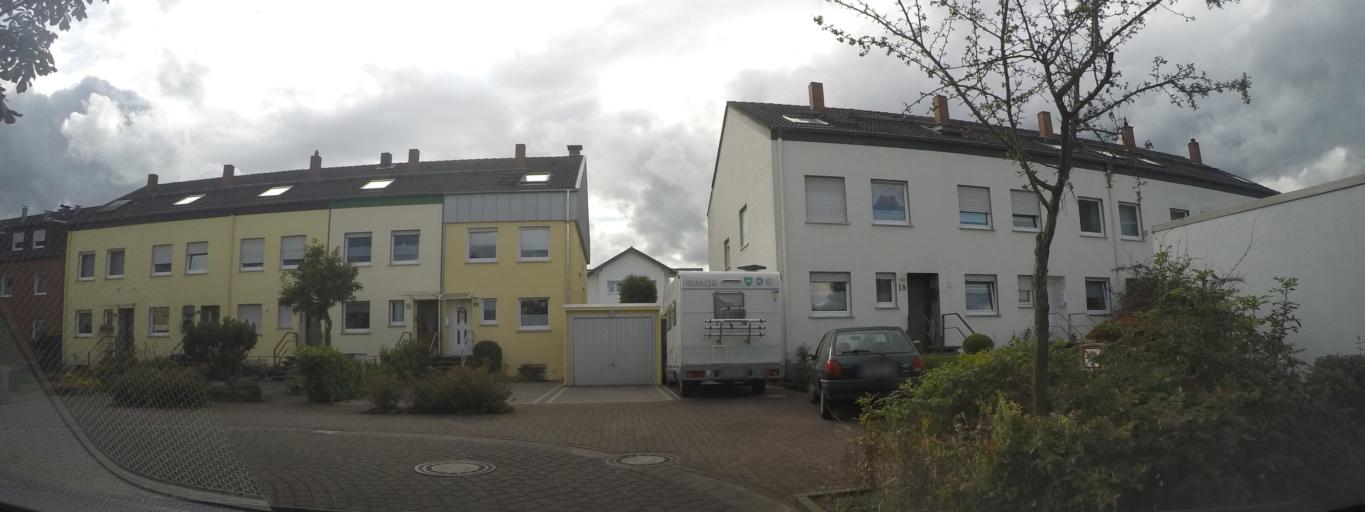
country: DE
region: North Rhine-Westphalia
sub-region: Regierungsbezirk Arnsberg
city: Lippstadt
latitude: 51.6859
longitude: 8.3495
